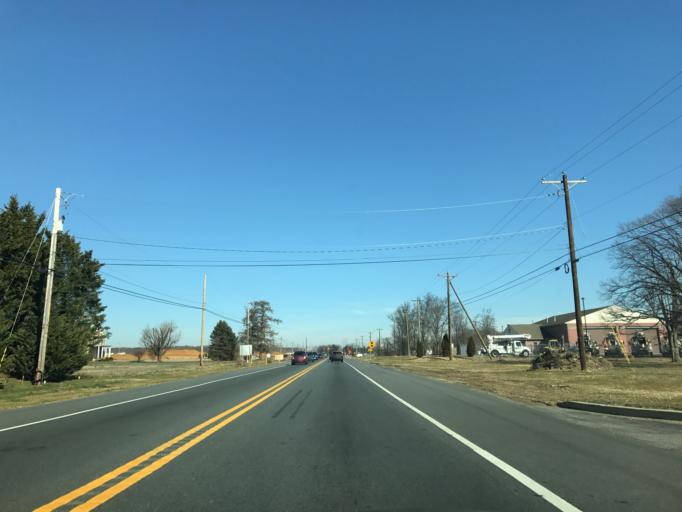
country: US
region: Delaware
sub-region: New Castle County
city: Middletown
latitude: 39.4765
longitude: -75.7205
